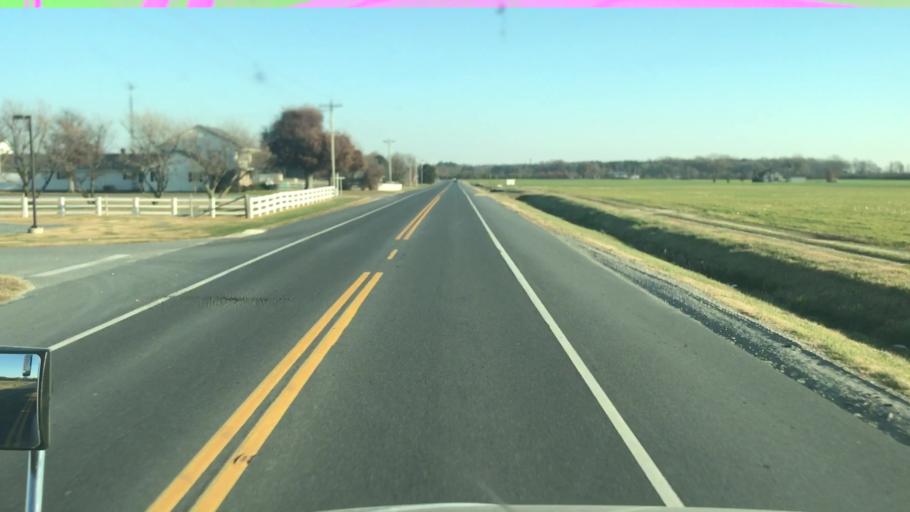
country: US
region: Delaware
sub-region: Sussex County
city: Bridgeville
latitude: 38.7883
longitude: -75.6849
